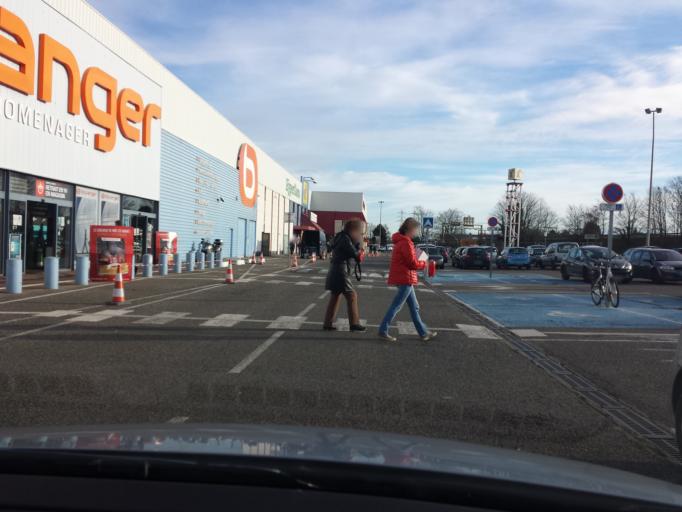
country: FR
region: Ile-de-France
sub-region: Departement de l'Essonne
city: Massy
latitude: 48.7232
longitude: 2.2740
